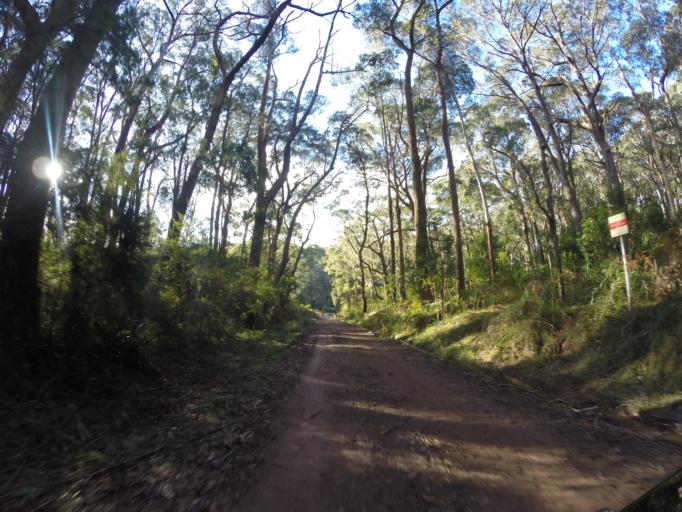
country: AU
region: New South Wales
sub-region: Wollongong
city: Cordeaux Heights
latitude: -34.4070
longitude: 150.7859
